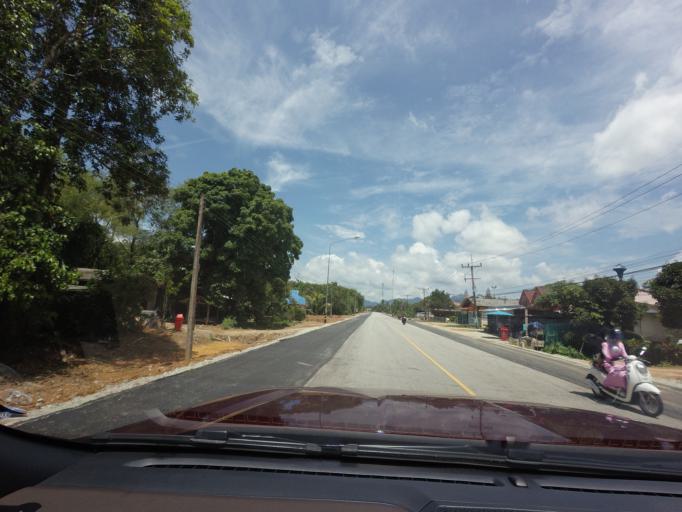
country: TH
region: Narathiwat
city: Ra-ngae
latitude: 6.2748
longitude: 101.6987
